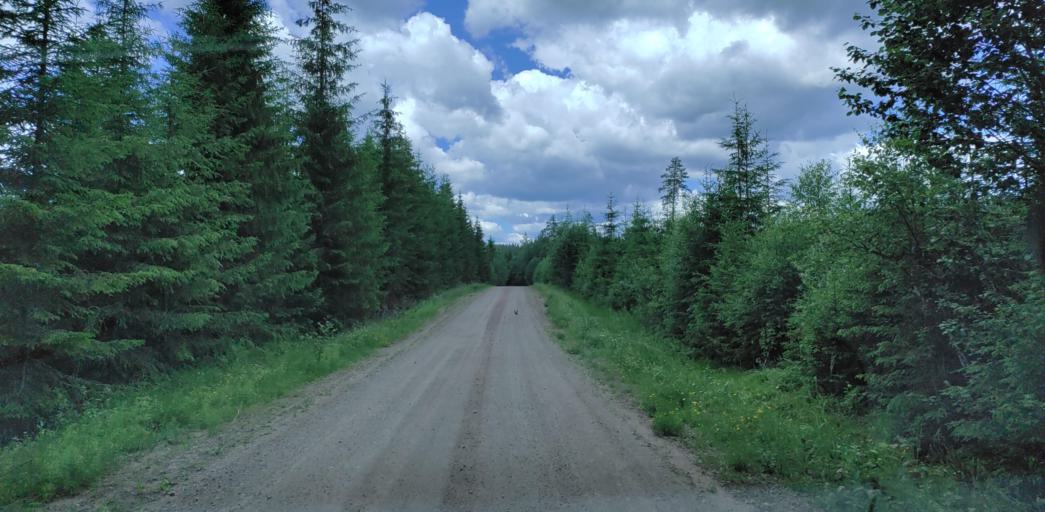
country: SE
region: Vaermland
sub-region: Hagfors Kommun
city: Ekshaerad
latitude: 60.0856
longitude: 13.4391
